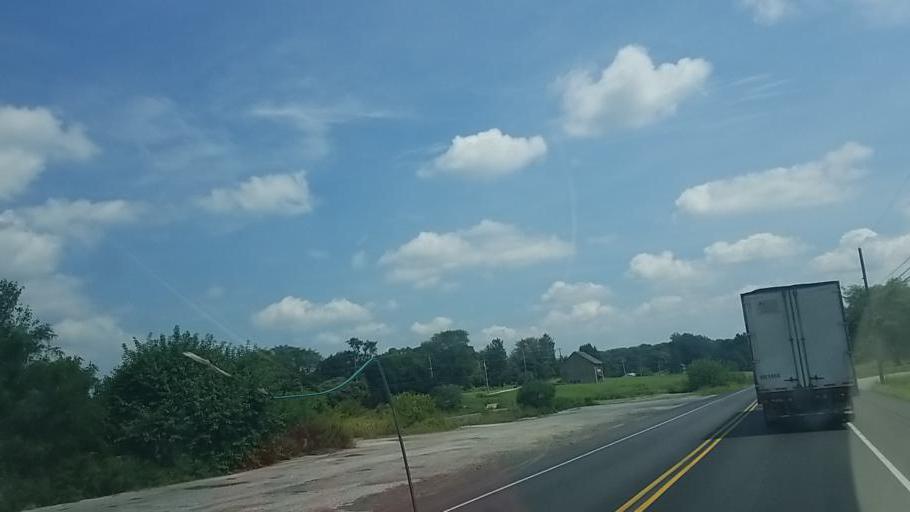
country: US
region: Pennsylvania
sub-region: Chester County
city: Toughkenamon
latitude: 39.8007
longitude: -75.7338
